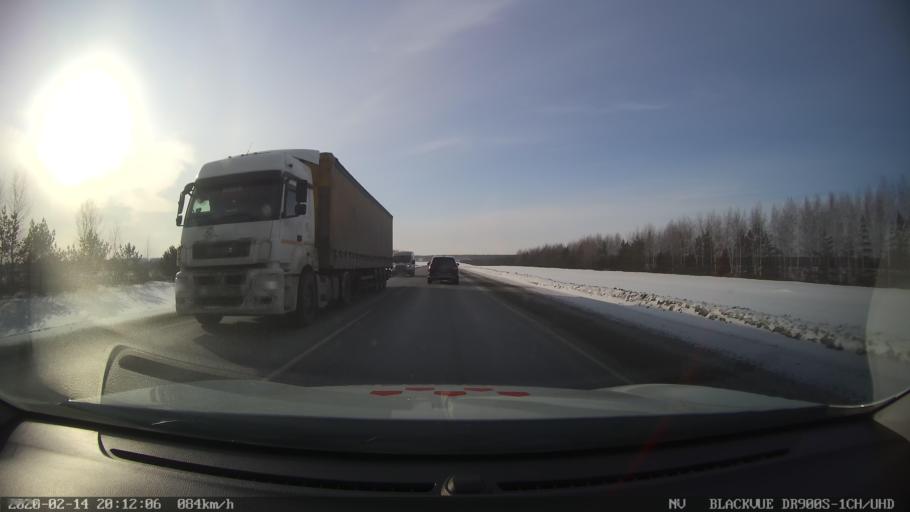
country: RU
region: Tatarstan
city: Verkhniy Uslon
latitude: 55.6697
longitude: 48.8662
